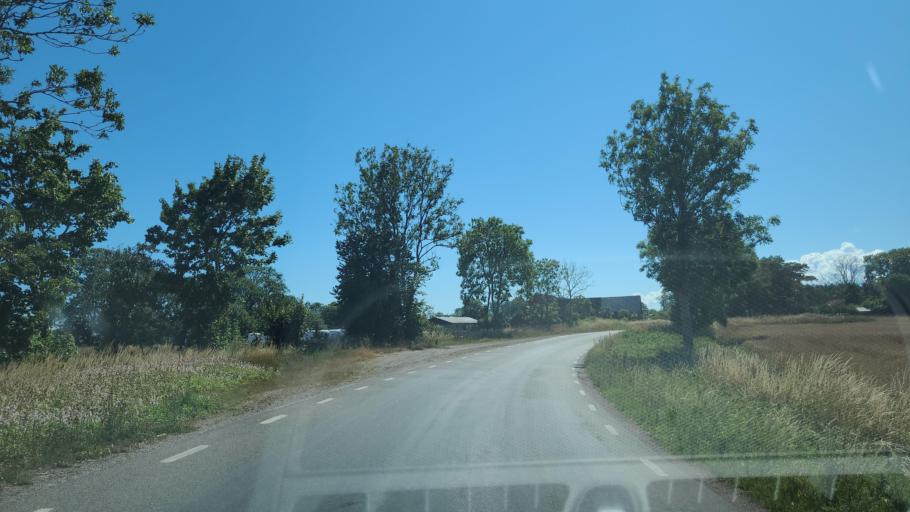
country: SE
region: Kalmar
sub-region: Borgholms Kommun
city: Borgholm
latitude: 56.7593
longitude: 16.7375
